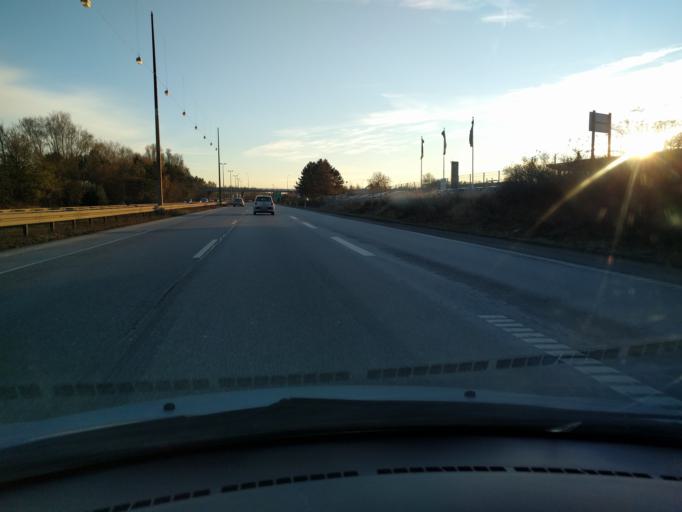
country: DK
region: Capital Region
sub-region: Ishoj Kommune
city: Ishoj
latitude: 55.6197
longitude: 12.3271
